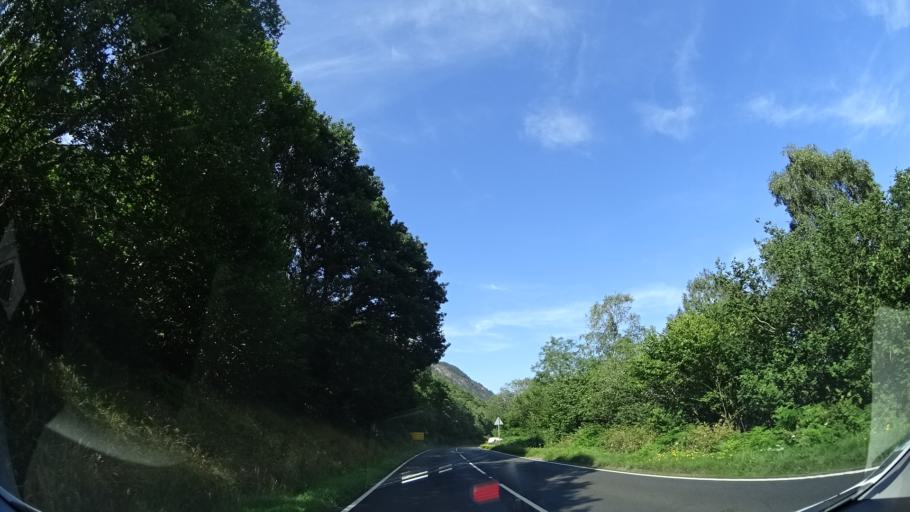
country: GB
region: Scotland
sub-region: Highland
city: Beauly
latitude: 57.3814
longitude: -4.3756
